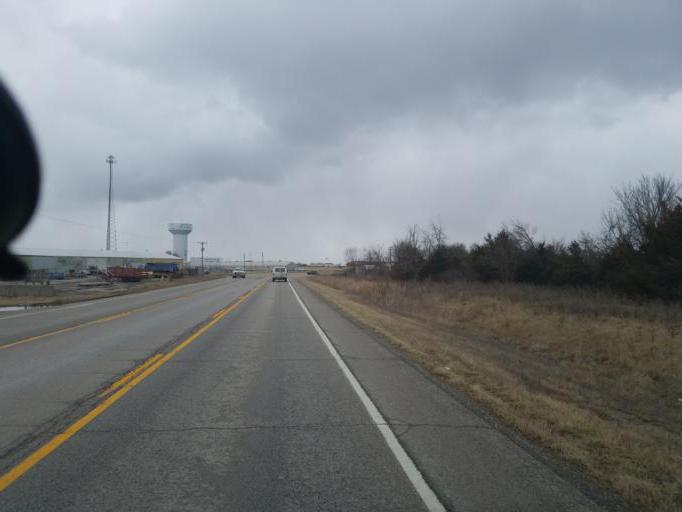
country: US
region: Missouri
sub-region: Macon County
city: Macon
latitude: 39.7652
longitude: -92.4687
